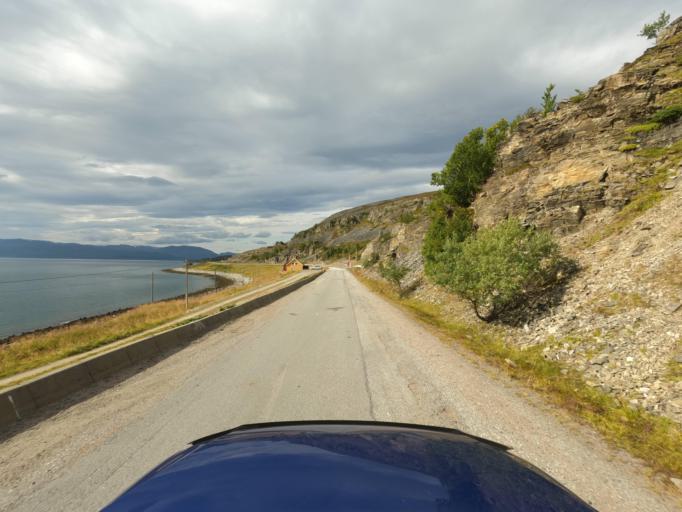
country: NO
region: Finnmark Fylke
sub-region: Kvalsund
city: Kvalsund
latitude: 70.5083
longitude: 23.8796
